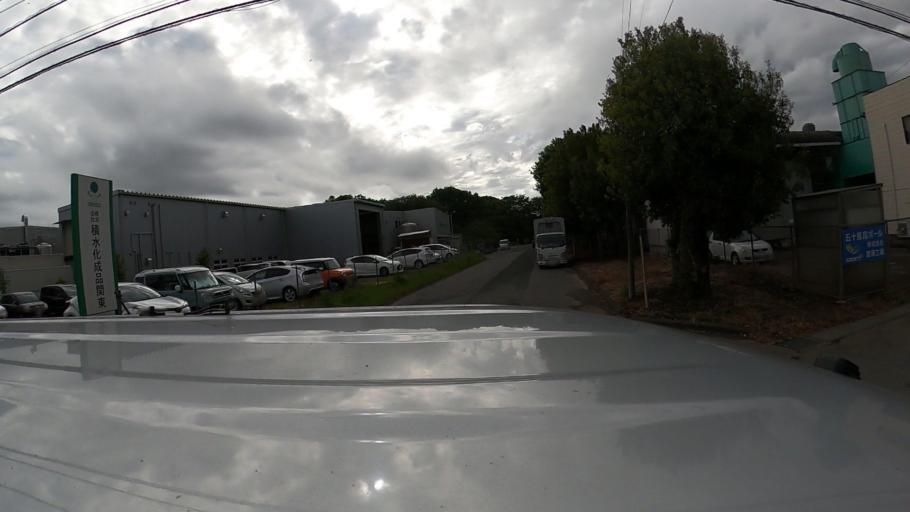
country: JP
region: Ibaraki
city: Inashiki
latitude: 36.0050
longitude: 140.2844
